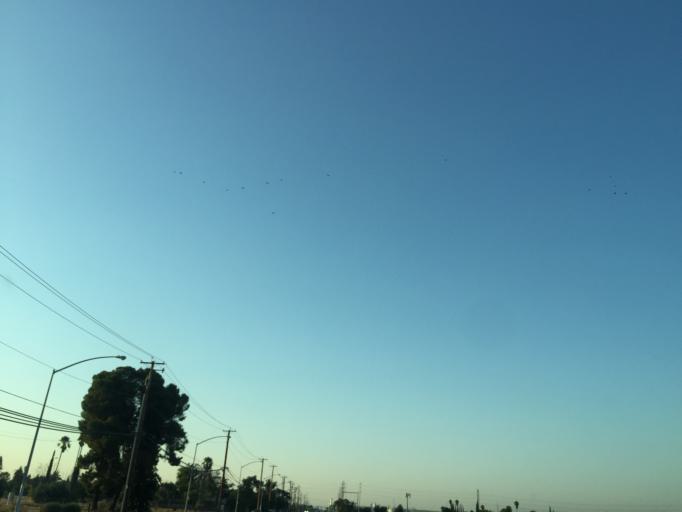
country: US
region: California
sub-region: Fresno County
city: Sunnyside
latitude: 36.7439
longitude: -119.7000
